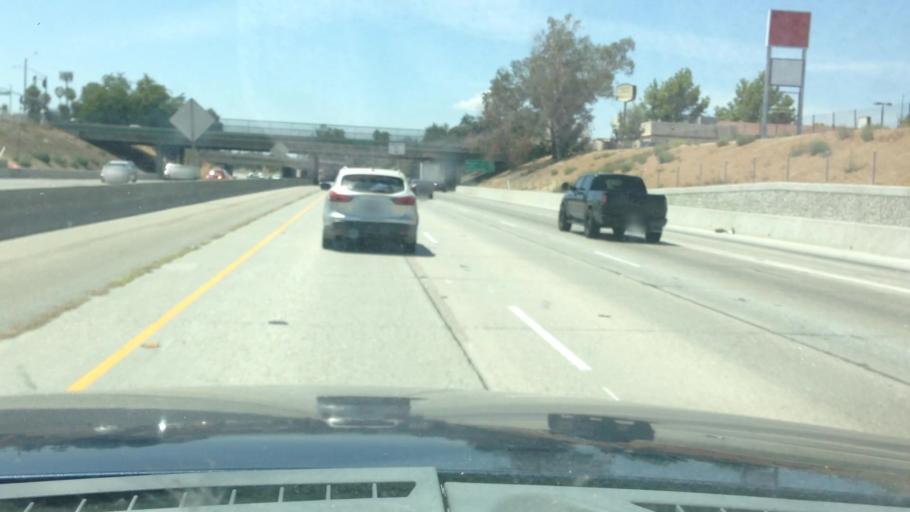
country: US
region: California
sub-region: Kern County
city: Bakersfield
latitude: 35.3337
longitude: -119.0397
